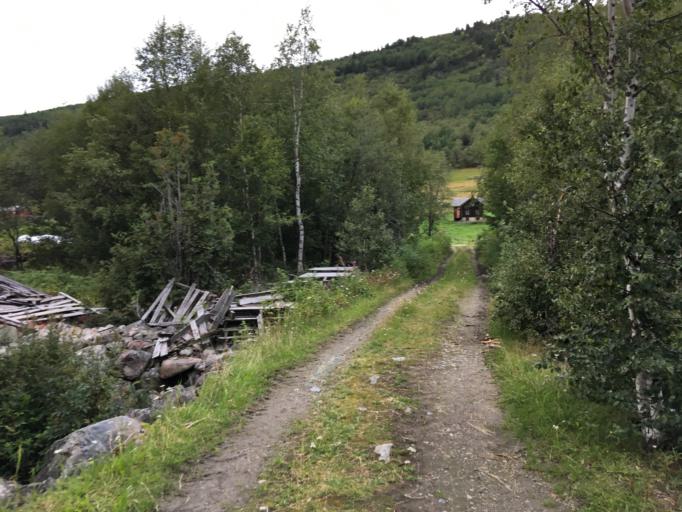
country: NO
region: Buskerud
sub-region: Hol
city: Hol
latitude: 60.6182
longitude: 8.2236
